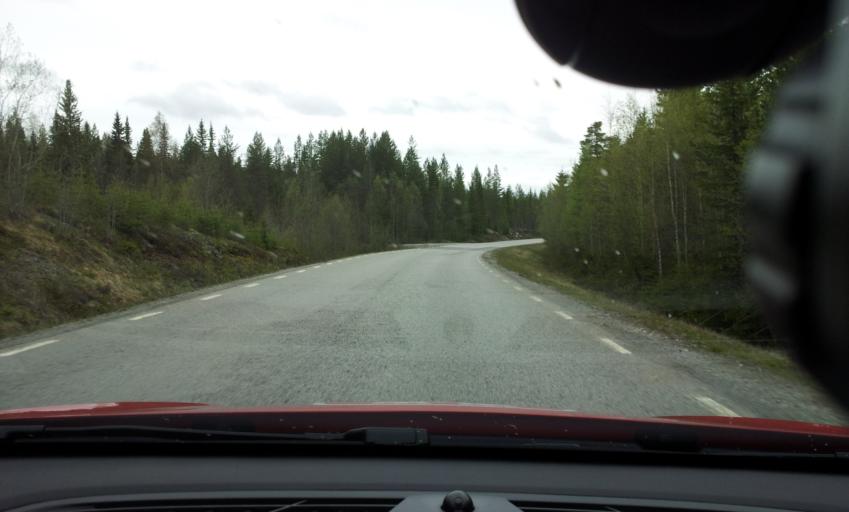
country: SE
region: Jaemtland
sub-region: Bergs Kommun
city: Hoverberg
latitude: 62.7545
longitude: 14.5671
